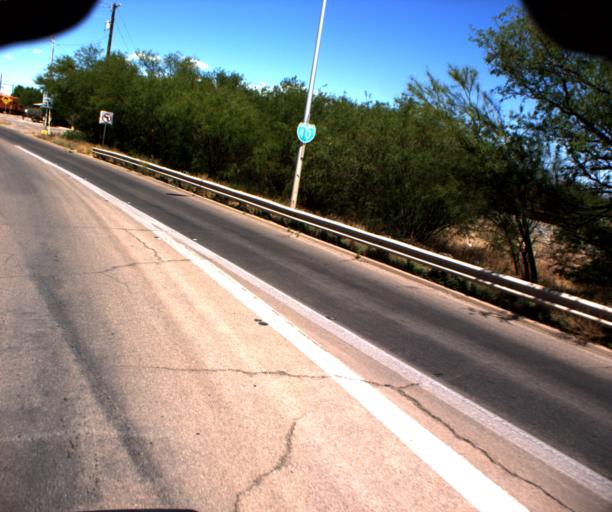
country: US
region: Arizona
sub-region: Cochise County
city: Benson
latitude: 31.9675
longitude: -110.2925
